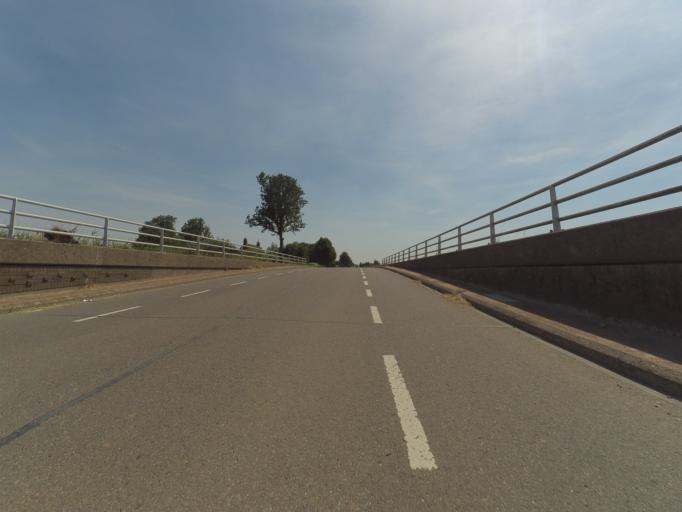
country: NL
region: North Brabant
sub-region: Gemeente Woensdrecht
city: Woensdrecht
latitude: 51.4348
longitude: 4.2957
